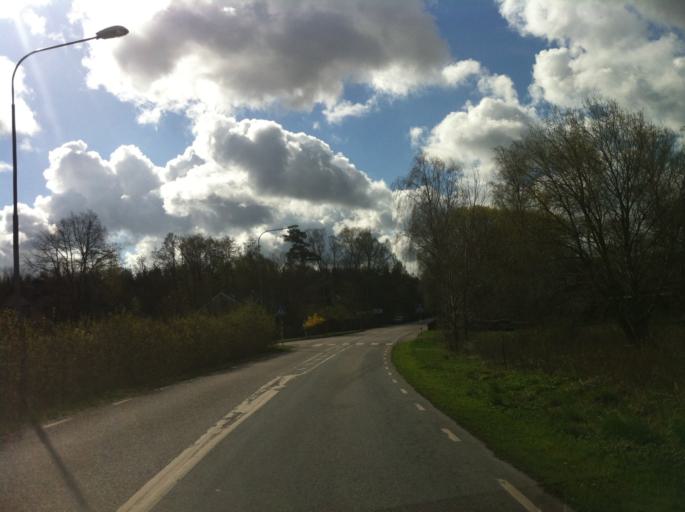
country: SE
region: Skane
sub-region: Hoors Kommun
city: Satofta
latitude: 55.9013
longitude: 13.6084
